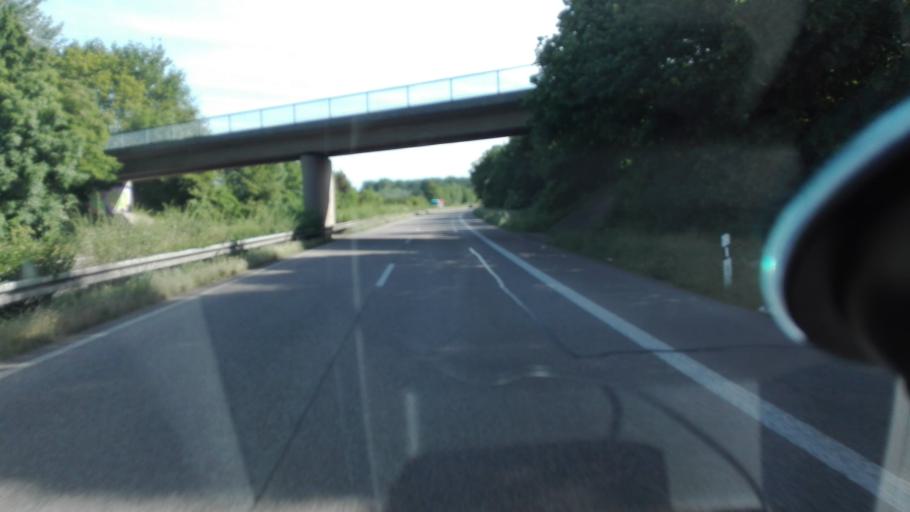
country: DE
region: Baden-Wuerttemberg
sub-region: Karlsruhe Region
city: Eggenstein-Leopoldshafen
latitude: 49.0541
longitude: 8.3684
